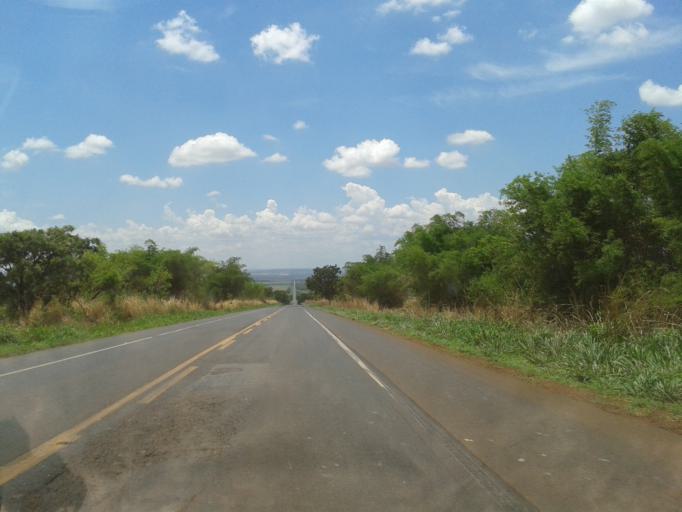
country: BR
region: Goias
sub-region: Goiatuba
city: Goiatuba
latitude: -18.2552
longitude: -49.6779
